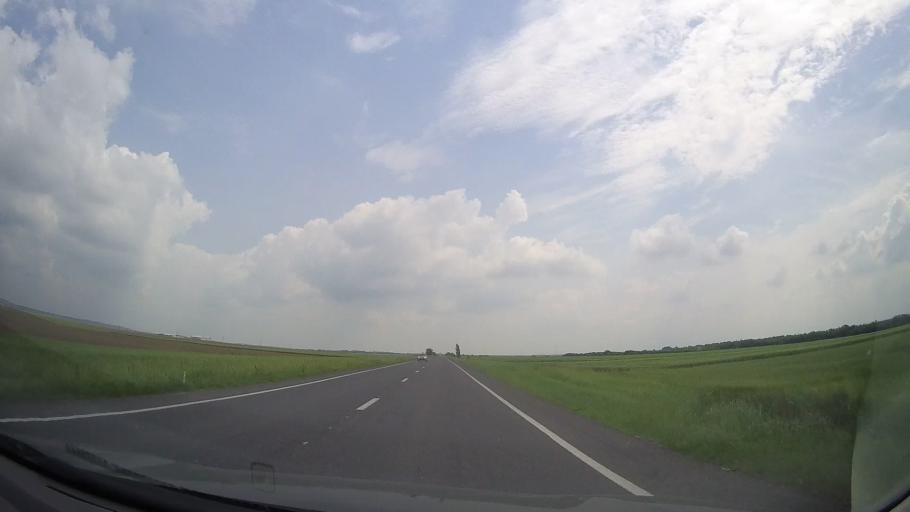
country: RO
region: Timis
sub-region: Comuna Topolovatu Mare
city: Topolovatu Mare
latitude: 45.7749
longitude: 21.6413
